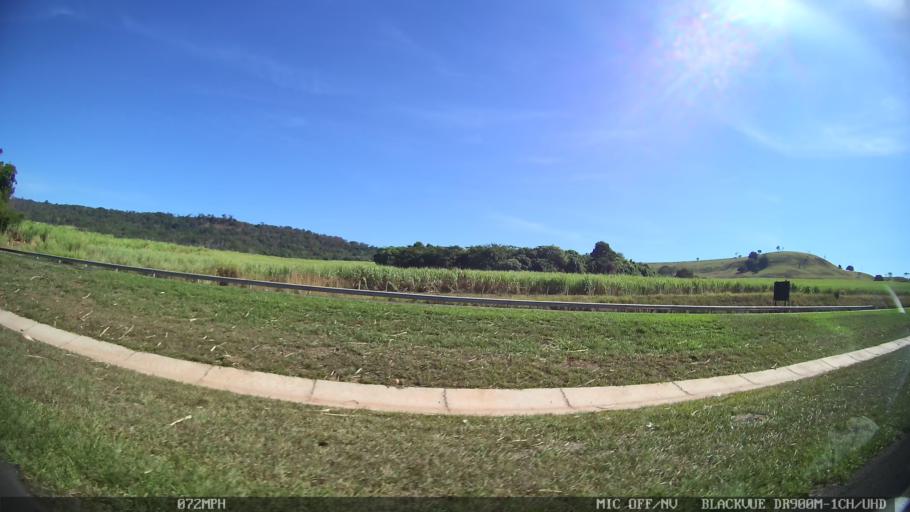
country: BR
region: Sao Paulo
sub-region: Sao Simao
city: Sao Simao
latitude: -21.4841
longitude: -47.6408
